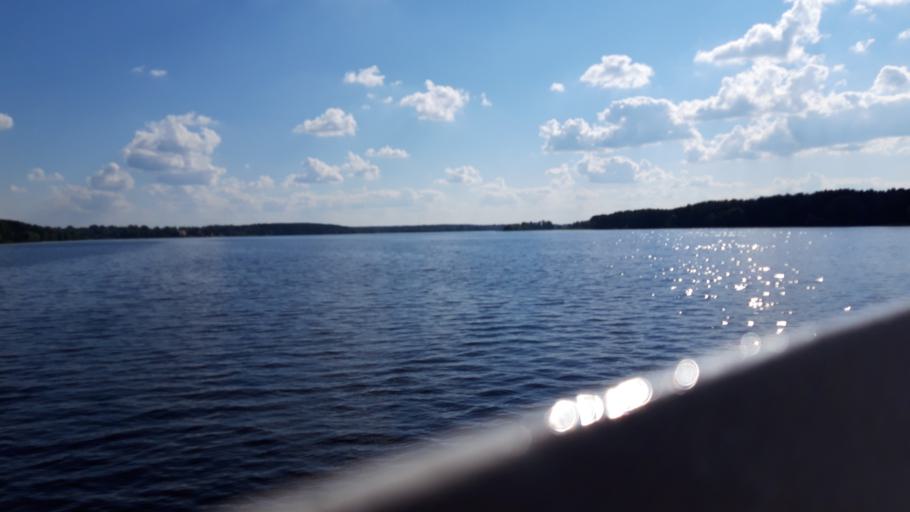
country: RU
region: Tverskaya
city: Zavidovo
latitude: 56.6284
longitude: 36.6012
